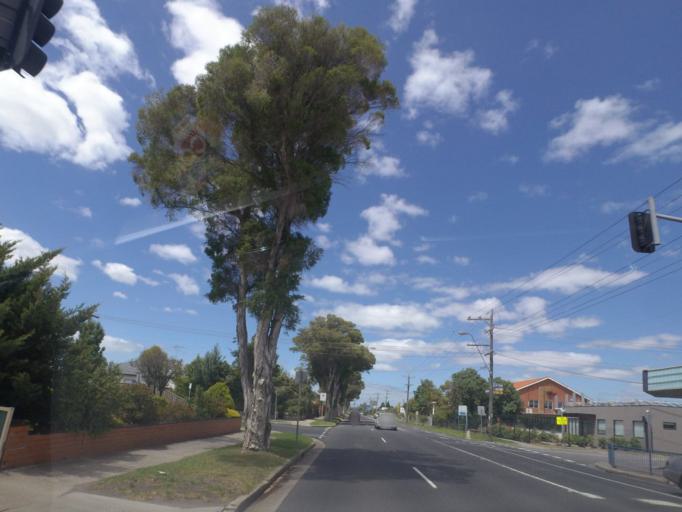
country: AU
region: Victoria
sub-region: Brimbank
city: Sunshine North
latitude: -37.7694
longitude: 144.8302
